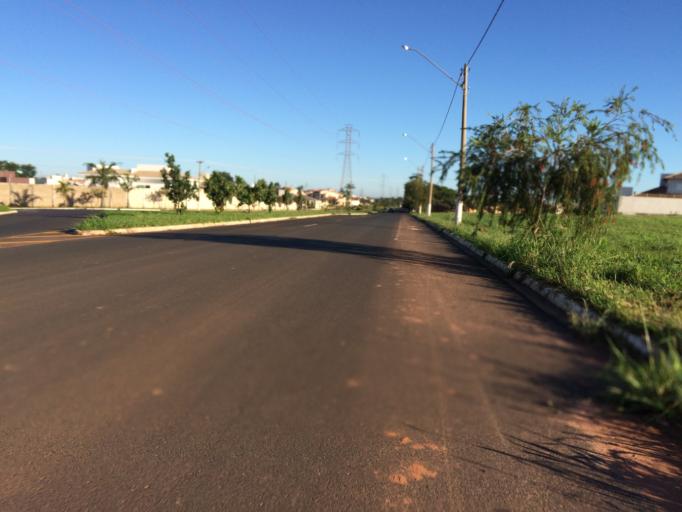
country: BR
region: Sao Paulo
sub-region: Matao
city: Matao
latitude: -21.6239
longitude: -48.3599
